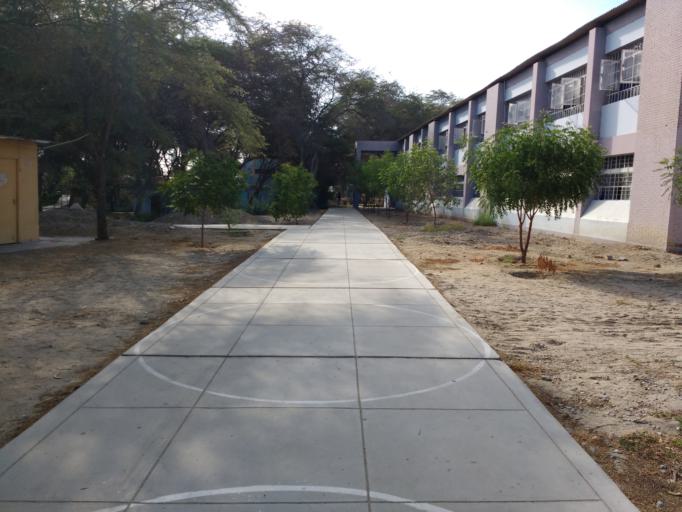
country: PE
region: Piura
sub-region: Provincia de Piura
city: Piura
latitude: -5.1805
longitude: -80.6216
